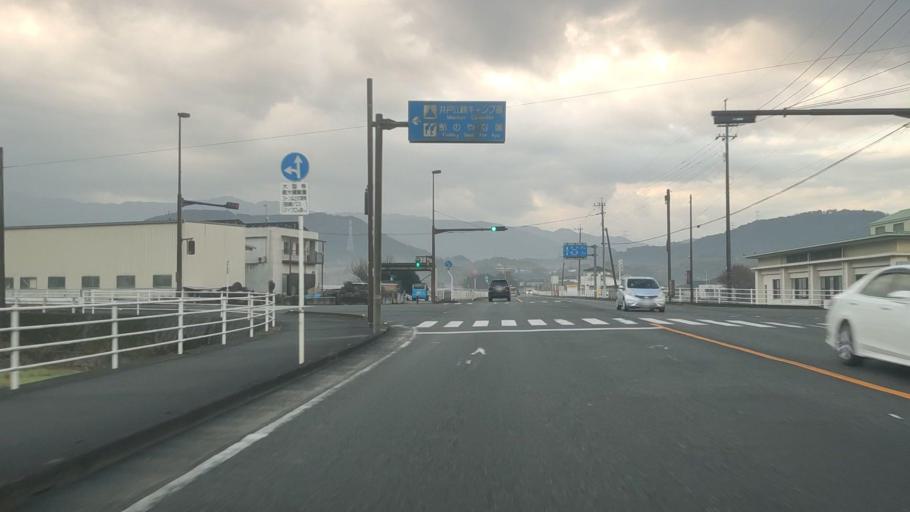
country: JP
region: Kumamoto
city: Matsubase
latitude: 32.6482
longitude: 130.8114
